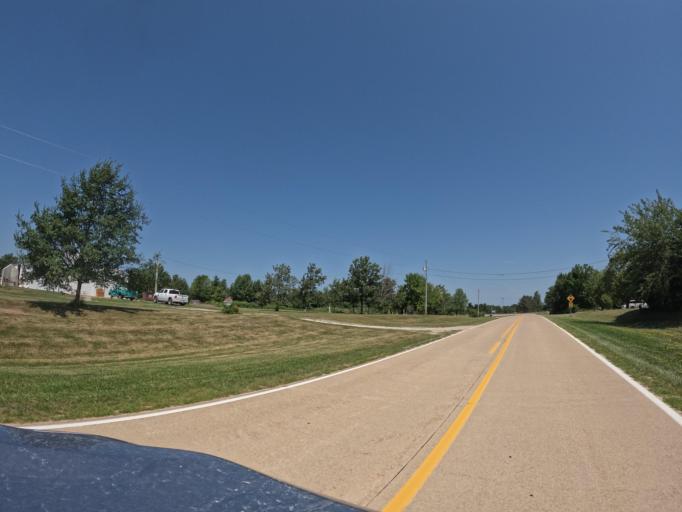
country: US
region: Iowa
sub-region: Henry County
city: Mount Pleasant
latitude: 40.8843
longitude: -91.5603
